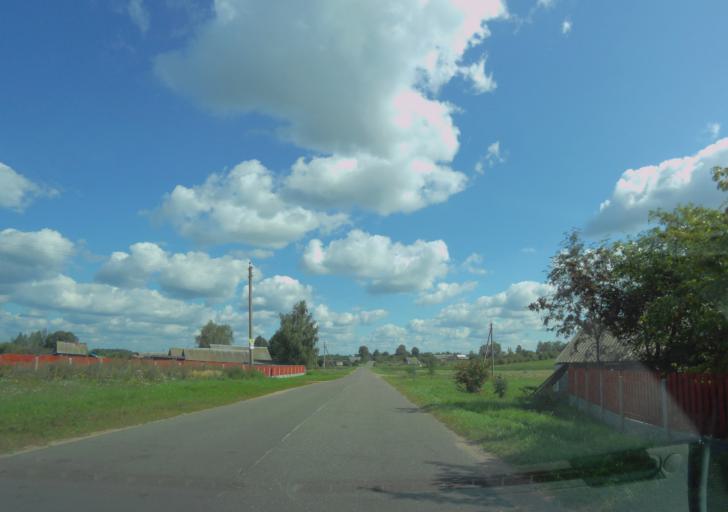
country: BY
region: Minsk
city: Zyembin
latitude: 54.4237
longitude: 28.4180
